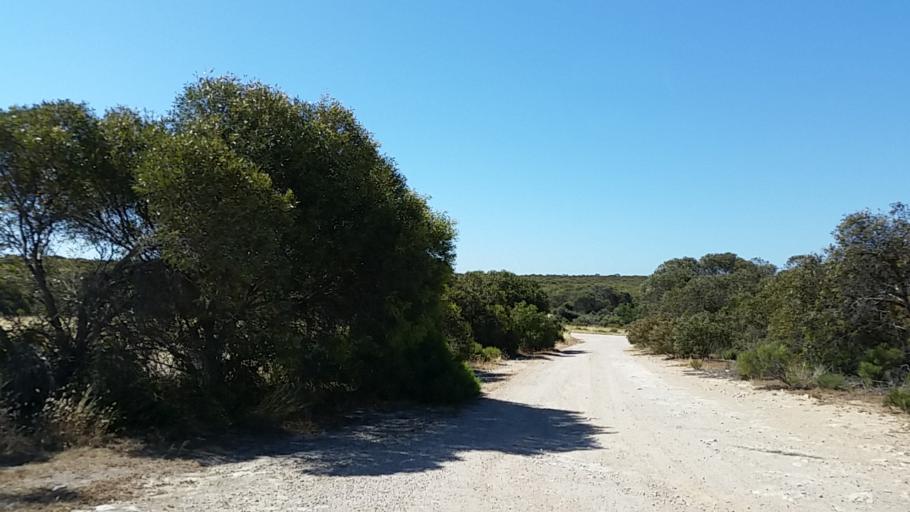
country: AU
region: South Australia
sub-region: Yorke Peninsula
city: Honiton
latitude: -35.2309
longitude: 137.1248
